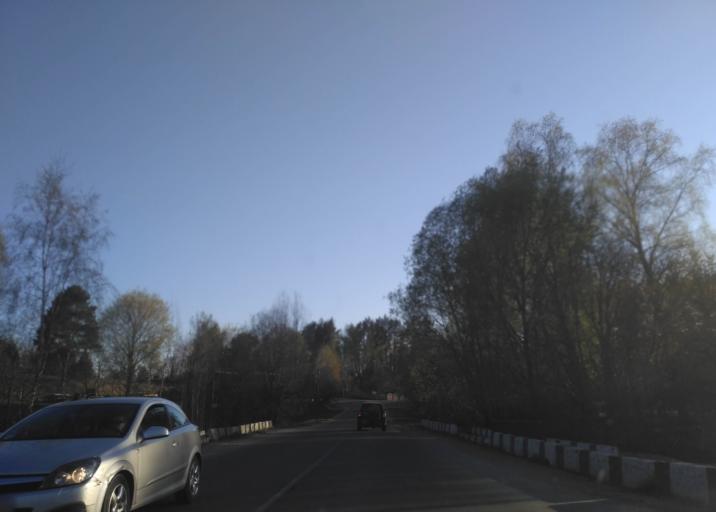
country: BY
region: Minsk
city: Pyatryshki
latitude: 54.1180
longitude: 27.1943
